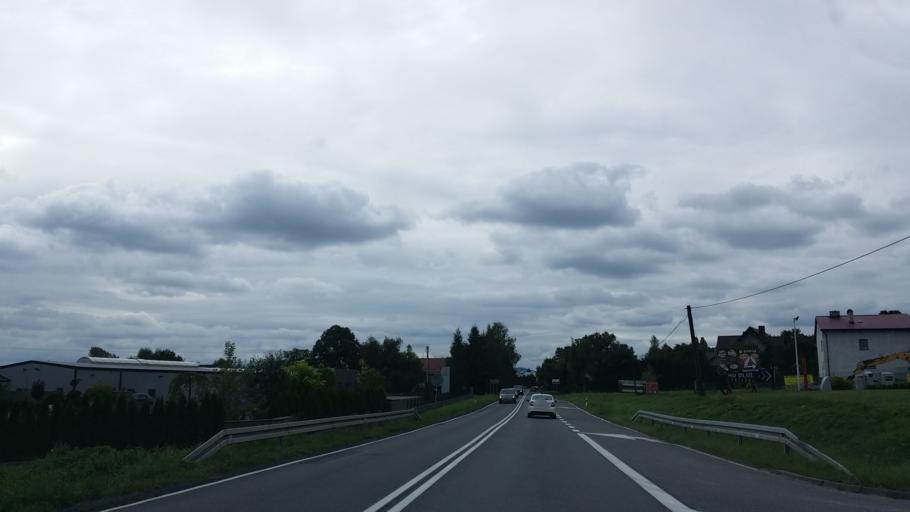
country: PL
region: Lesser Poland Voivodeship
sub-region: Powiat wadowicki
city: Radocza
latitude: 49.9188
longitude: 19.4811
